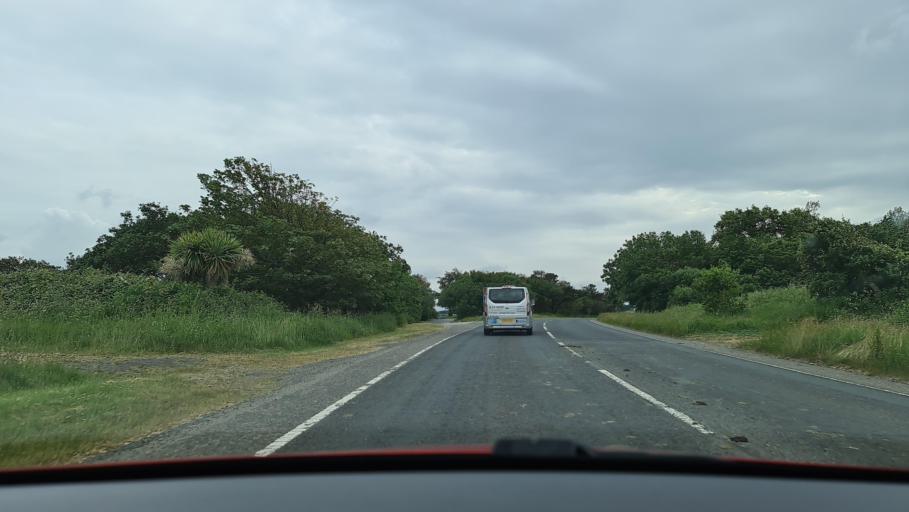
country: GB
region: England
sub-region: Cornwall
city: Poundstock
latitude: 50.7848
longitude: -4.5350
